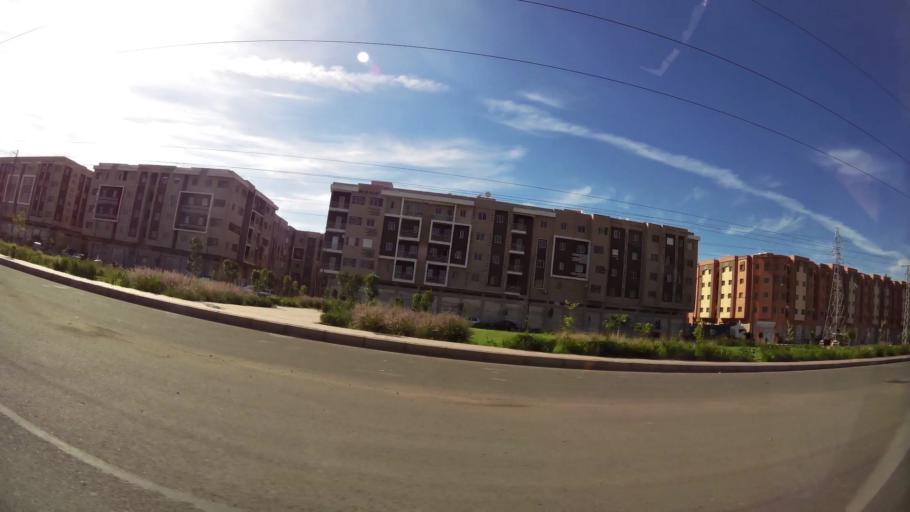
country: MA
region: Marrakech-Tensift-Al Haouz
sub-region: Marrakech
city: Marrakesh
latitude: 31.6479
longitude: -8.0366
